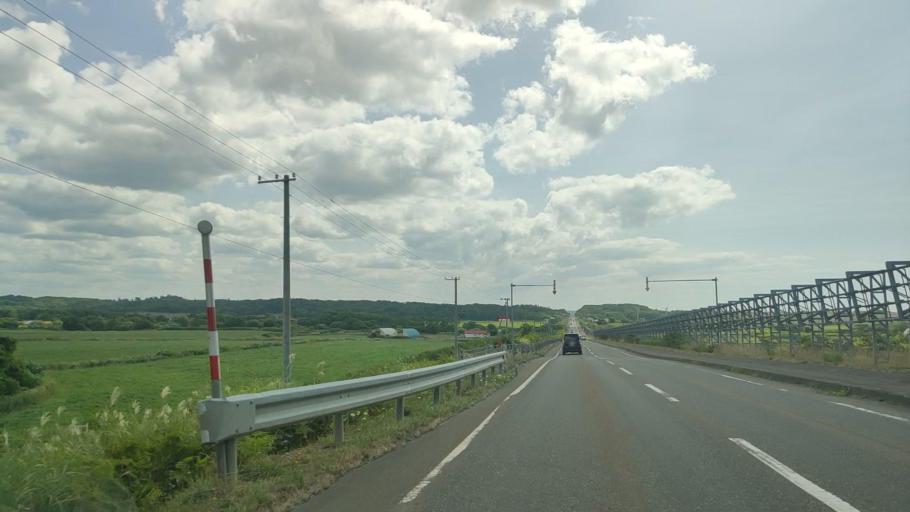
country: JP
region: Hokkaido
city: Makubetsu
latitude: 44.7785
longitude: 141.7913
